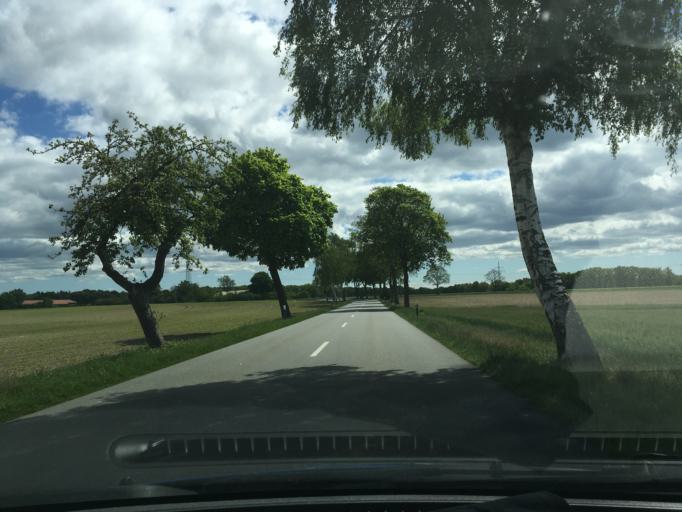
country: DE
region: Lower Saxony
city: Suderburg
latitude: 52.9206
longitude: 10.5024
